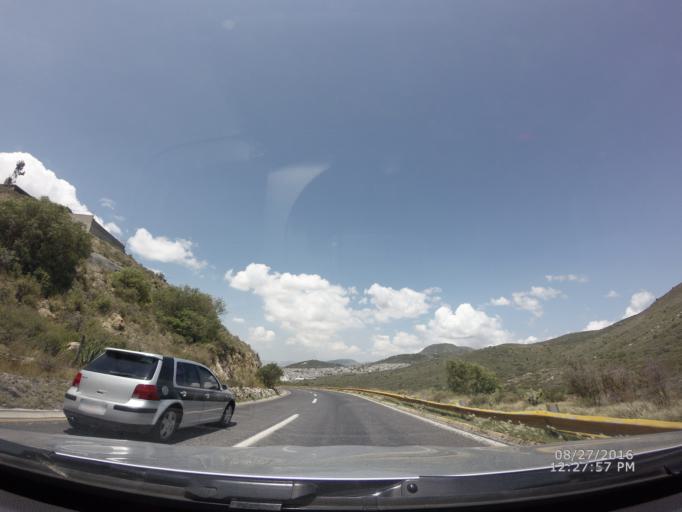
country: MX
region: Hidalgo
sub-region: Mineral de la Reforma
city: Colonia Militar
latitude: 20.1213
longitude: -98.6988
